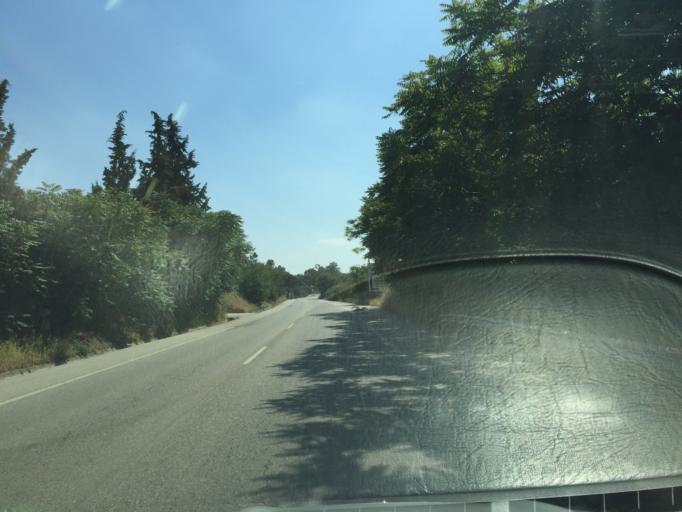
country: PT
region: Santarem
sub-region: Golega
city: Golega
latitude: 39.3827
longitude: -8.4523
